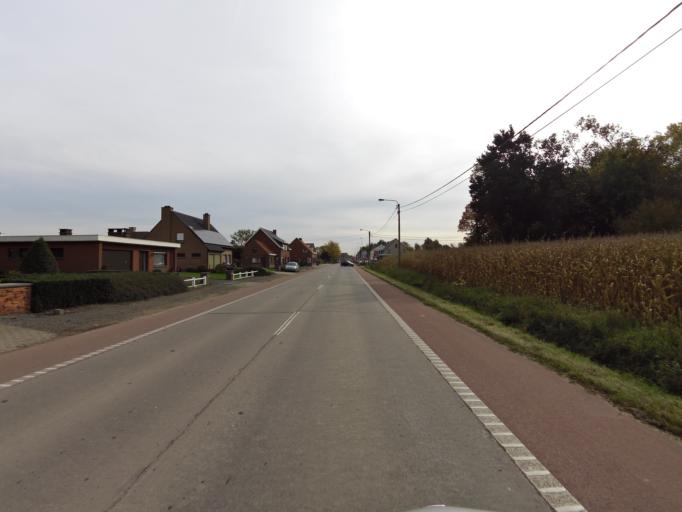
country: BE
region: Flanders
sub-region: Provincie West-Vlaanderen
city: Torhout
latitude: 51.0637
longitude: 3.1308
